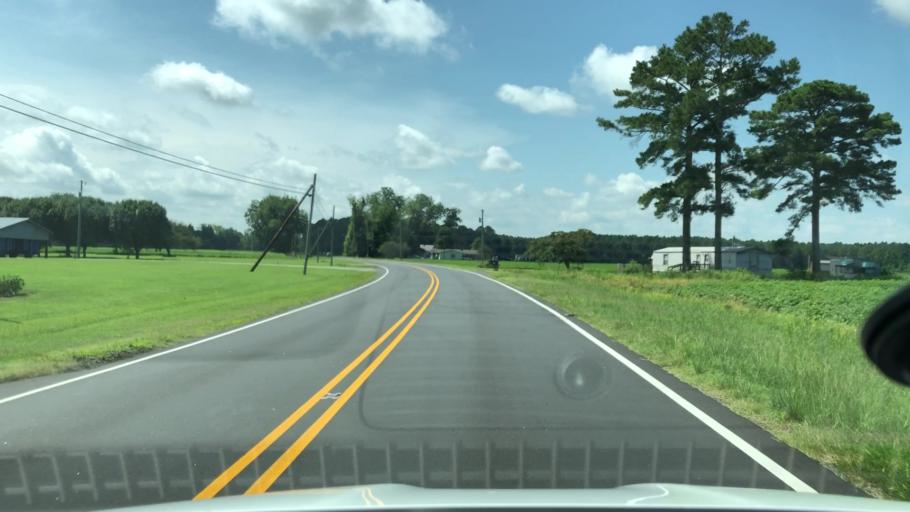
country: US
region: North Carolina
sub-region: Martin County
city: Williamston
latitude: 35.7640
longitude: -77.0742
